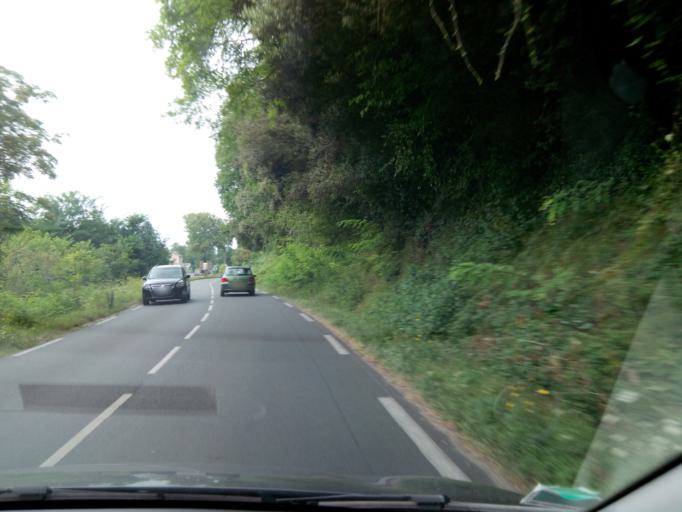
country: FR
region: Aquitaine
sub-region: Departement de la Dordogne
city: Eyvigues-et-Eybenes
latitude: 44.8727
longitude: 1.3654
